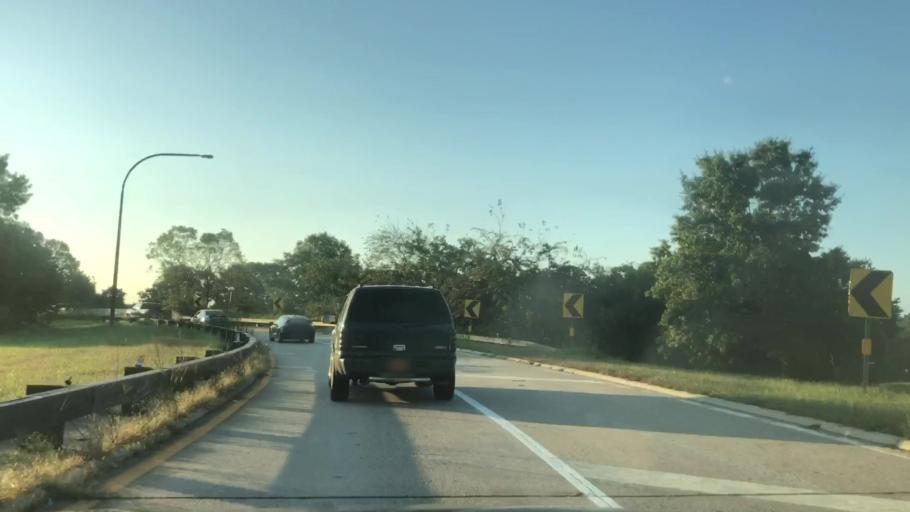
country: US
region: New York
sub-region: Nassau County
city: North Wantagh
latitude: 40.6976
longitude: -73.5199
